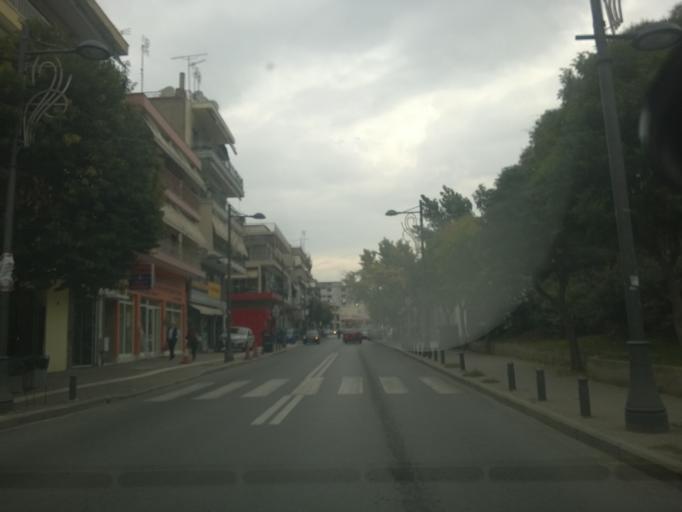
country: GR
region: Central Macedonia
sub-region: Nomos Thessalonikis
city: Stavroupoli
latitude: 40.6718
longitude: 22.9338
